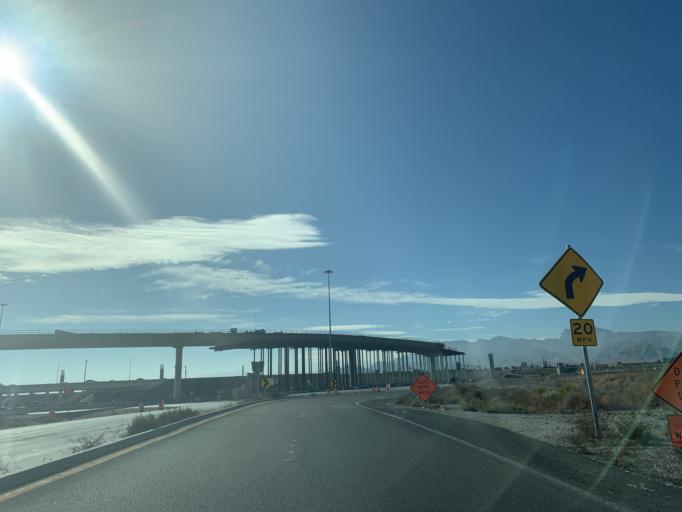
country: US
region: Nevada
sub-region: Clark County
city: Las Vegas
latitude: 36.2801
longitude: -115.2670
